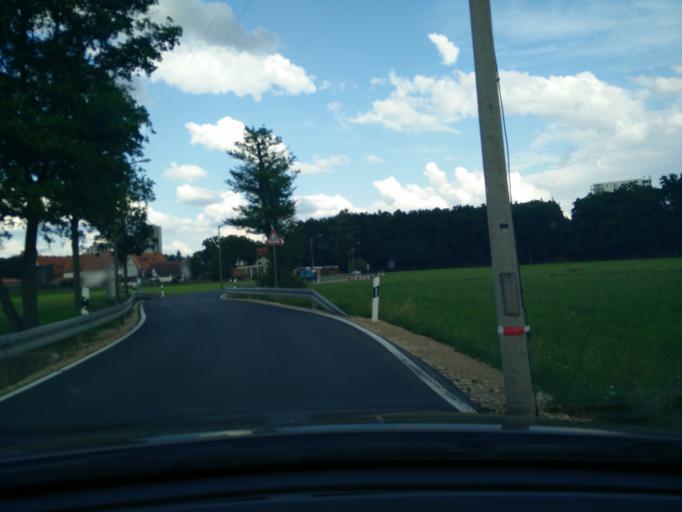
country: DE
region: Bavaria
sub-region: Regierungsbezirk Mittelfranken
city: Stein
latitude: 49.3888
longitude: 11.0268
